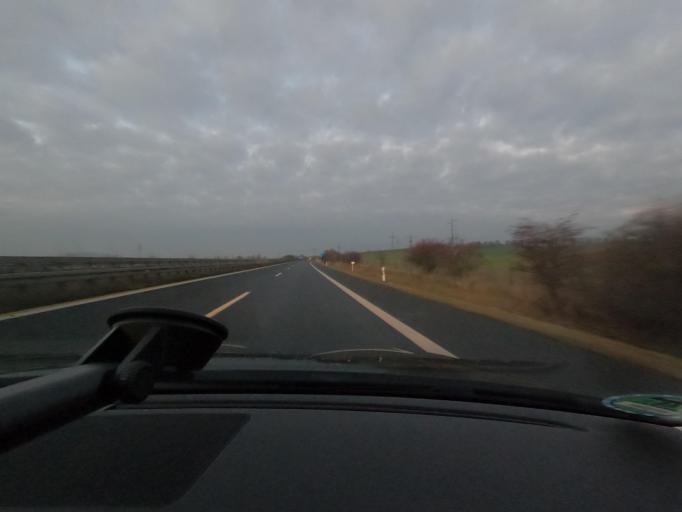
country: DE
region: Bavaria
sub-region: Upper Franconia
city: Ebensfeld
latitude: 50.0506
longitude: 10.9607
